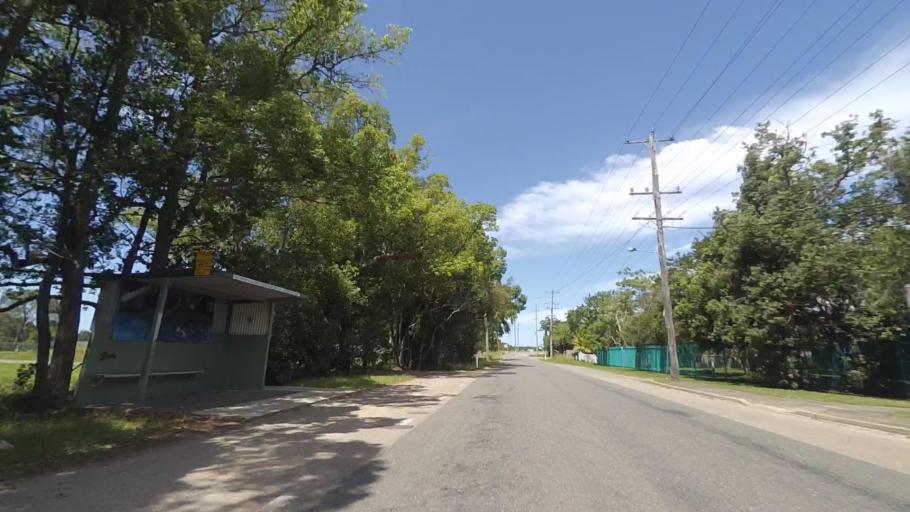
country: AU
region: New South Wales
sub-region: Port Stephens Shire
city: Anna Bay
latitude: -32.7662
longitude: 152.0107
